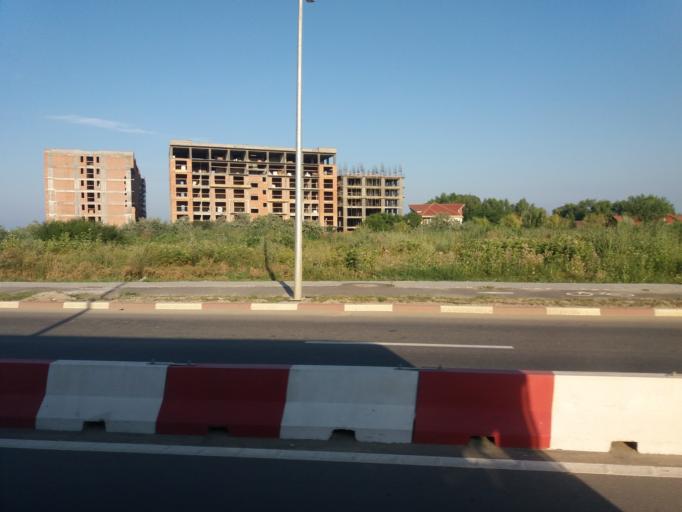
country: RO
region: Constanta
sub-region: Comuna Navodari
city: Navodari
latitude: 44.2900
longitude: 28.6184
